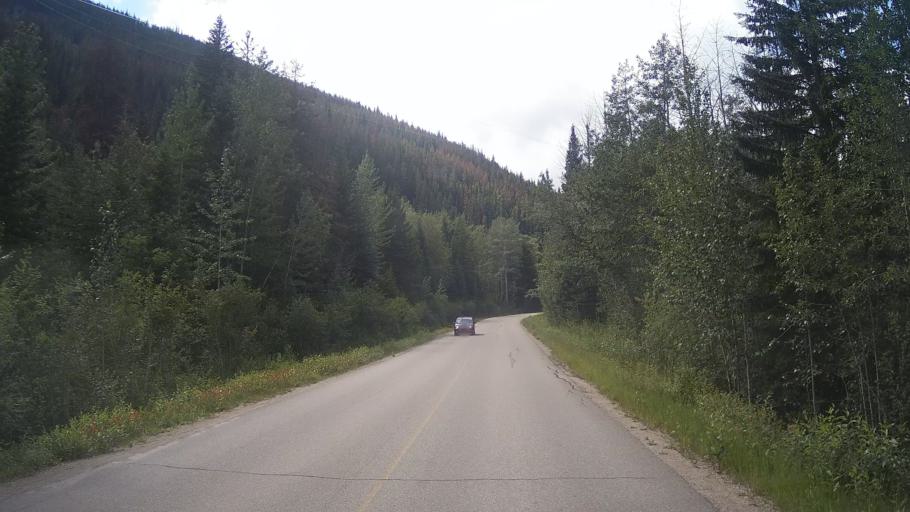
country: CA
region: Alberta
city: Jasper Park Lodge
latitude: 52.8512
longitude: -118.1197
